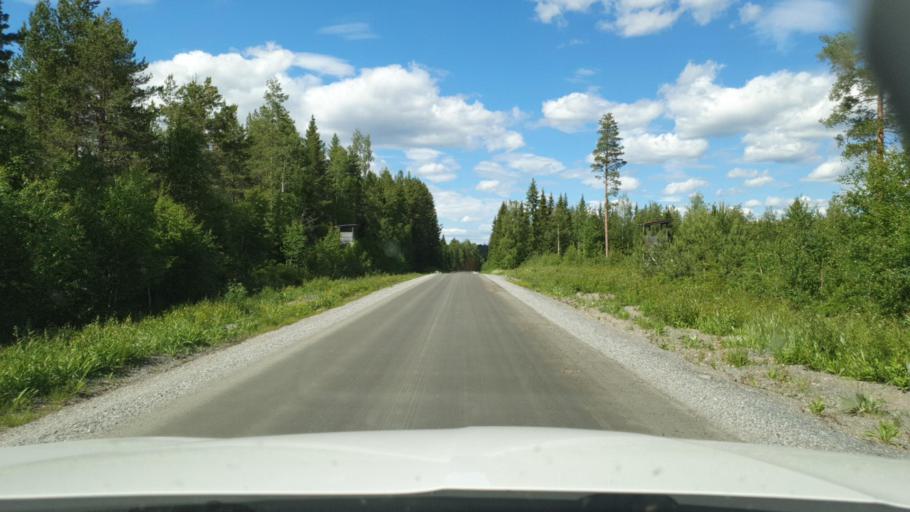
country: SE
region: Vaesterbotten
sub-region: Skelleftea Kommun
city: Forsbacka
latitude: 64.8077
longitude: 20.4986
